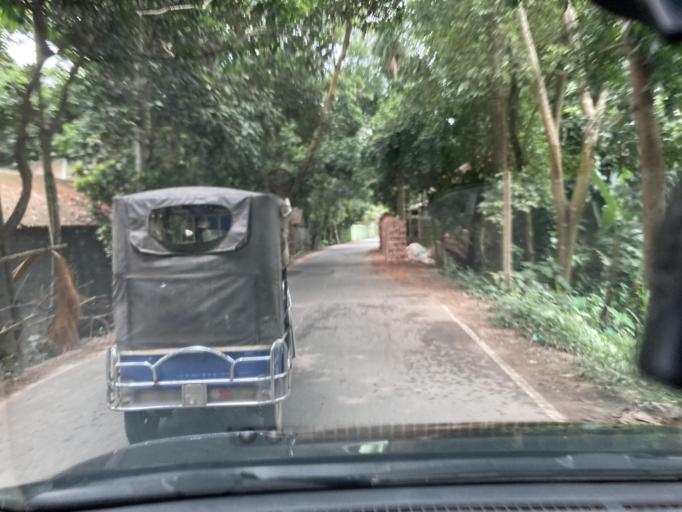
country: BD
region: Dhaka
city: Dohar
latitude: 23.7893
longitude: 90.0620
